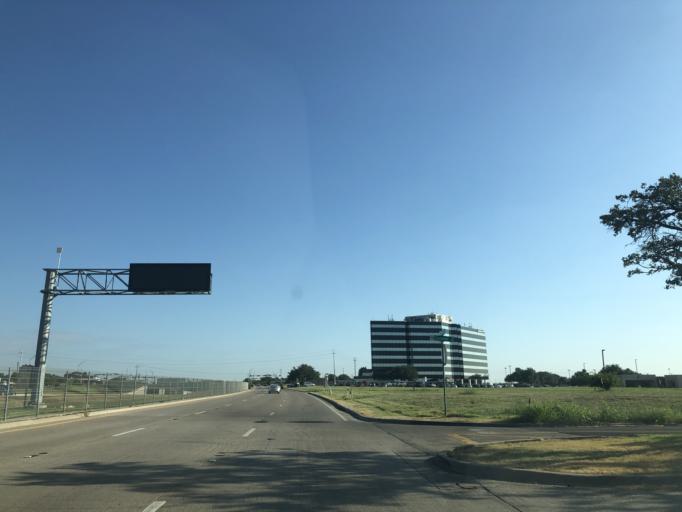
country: US
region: Texas
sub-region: Dallas County
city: Grand Prairie
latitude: 32.7378
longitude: -97.0192
